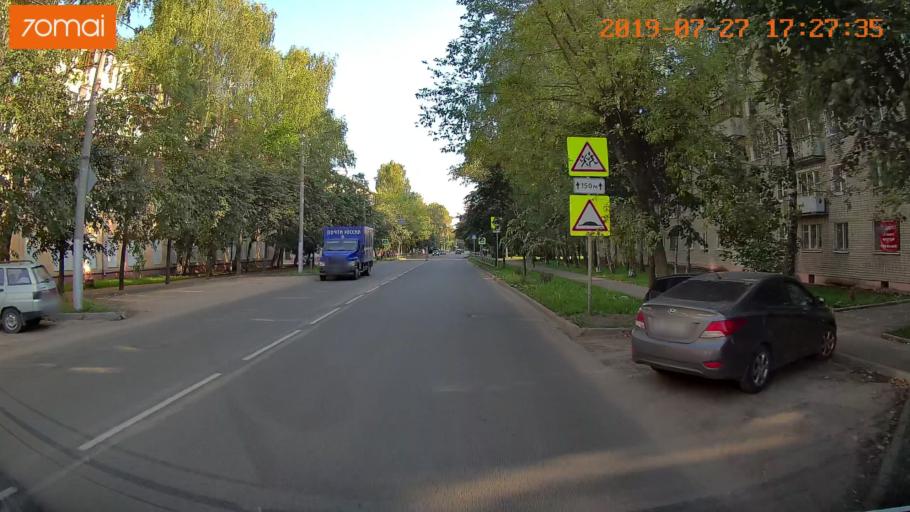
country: RU
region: Ivanovo
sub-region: Gorod Ivanovo
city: Ivanovo
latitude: 57.0135
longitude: 40.9785
